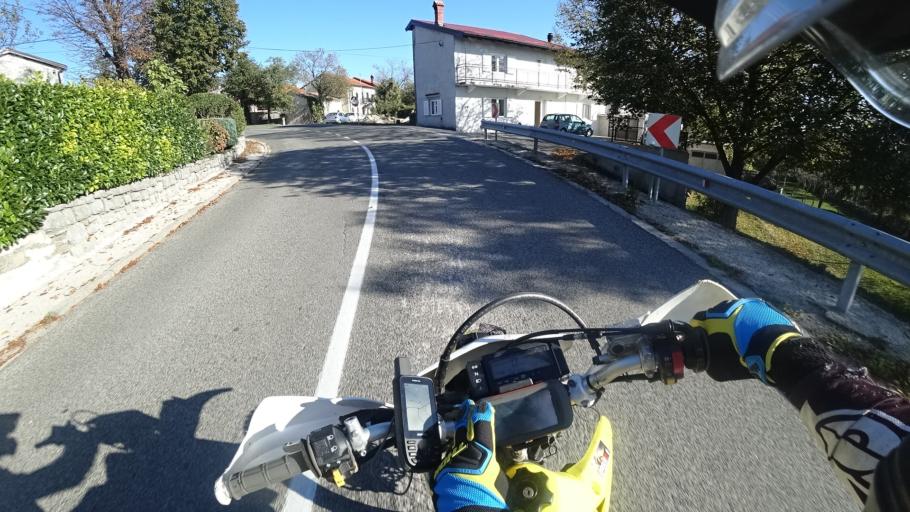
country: HR
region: Primorsko-Goranska
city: Klana
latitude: 45.4451
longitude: 14.3364
